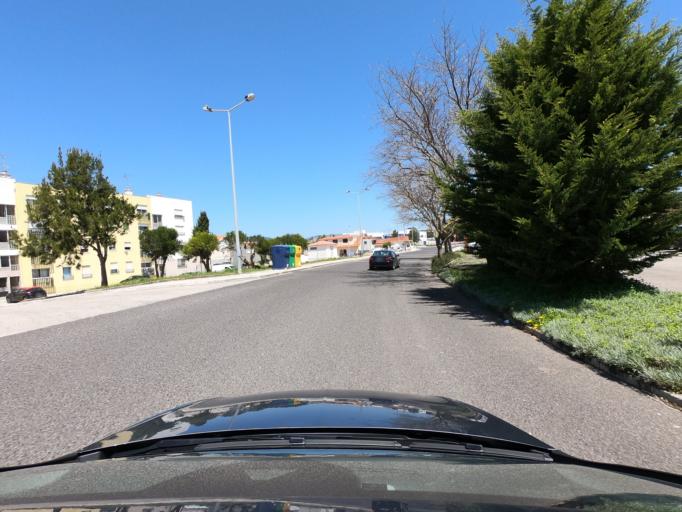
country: PT
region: Lisbon
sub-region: Cascais
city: Parede
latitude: 38.7276
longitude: -9.3612
